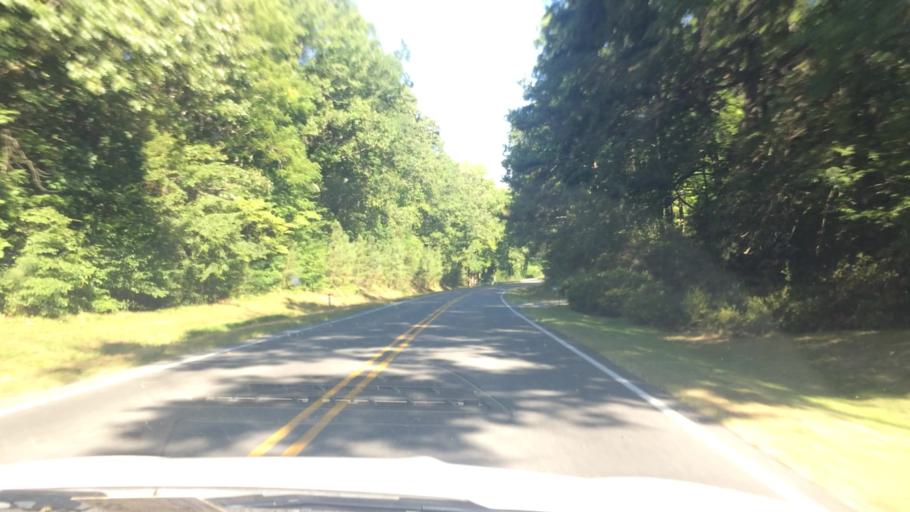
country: US
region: Virginia
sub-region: Lancaster County
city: Lancaster
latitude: 37.7990
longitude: -76.5276
